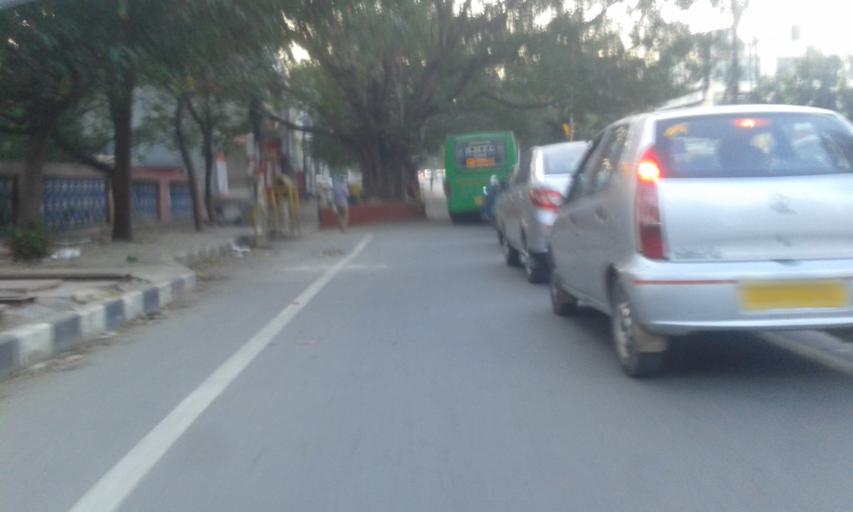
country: IN
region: Karnataka
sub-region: Bangalore Urban
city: Bangalore
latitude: 12.9613
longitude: 77.6363
